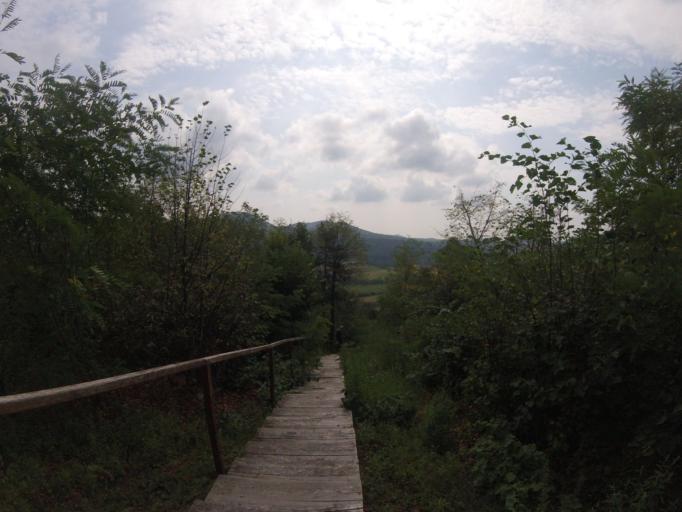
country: HU
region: Borsod-Abauj-Zemplen
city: Sarospatak
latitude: 48.4507
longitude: 21.5226
